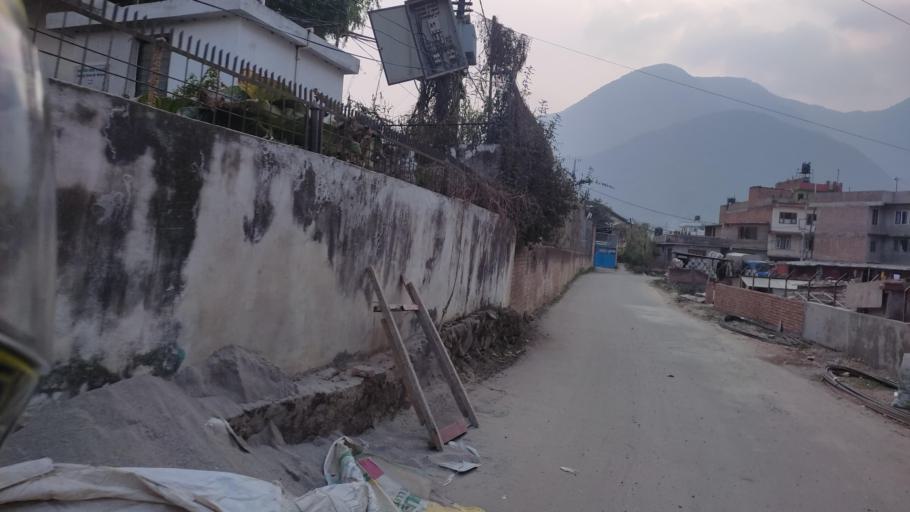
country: NP
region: Central Region
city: Kirtipur
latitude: 27.6686
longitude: 85.2752
